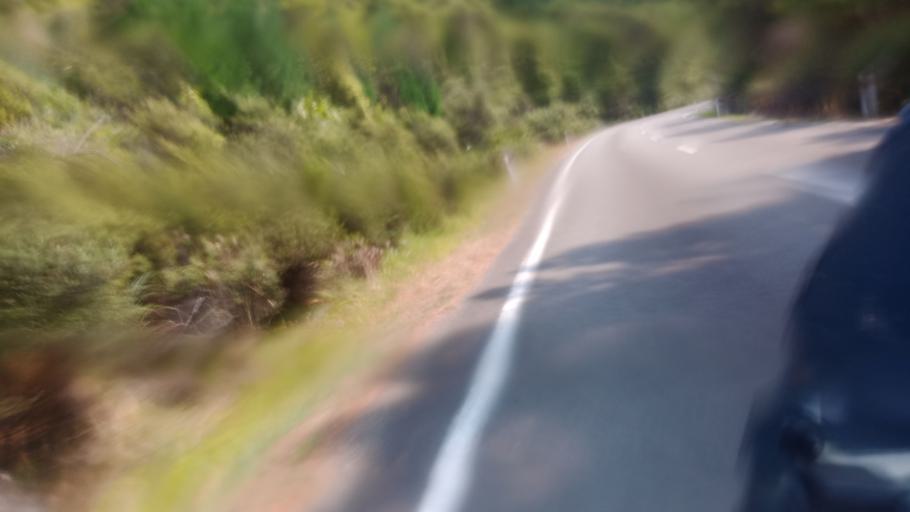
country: NZ
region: Bay of Plenty
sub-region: Opotiki District
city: Opotiki
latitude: -37.5788
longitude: 178.1307
